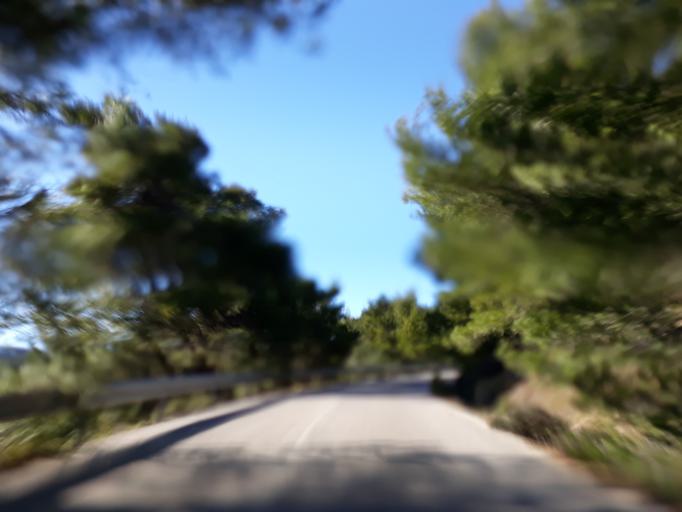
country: GR
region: Attica
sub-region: Nomarchia Dytikis Attikis
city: Fyli
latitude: 38.1450
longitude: 23.6408
